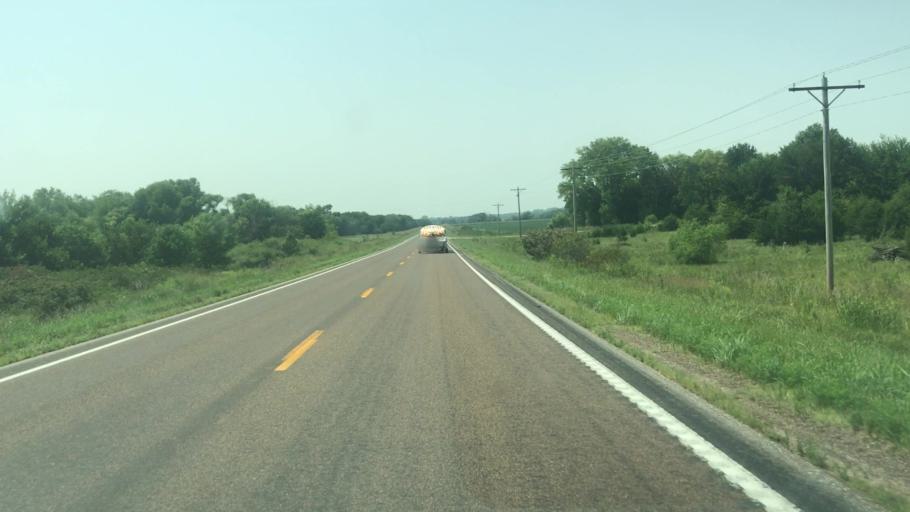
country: US
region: Nebraska
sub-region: Buffalo County
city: Ravenna
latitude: 41.0760
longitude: -98.6696
